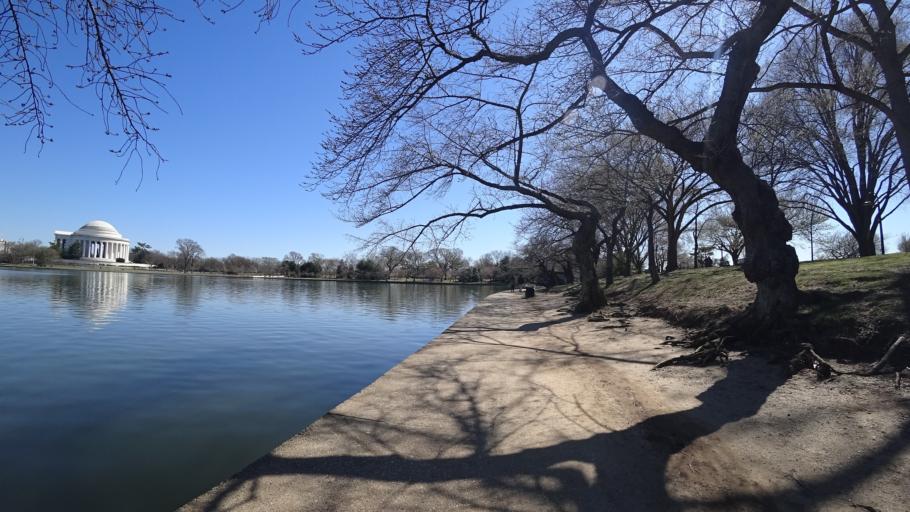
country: US
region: Washington, D.C.
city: Washington, D.C.
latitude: 38.8815
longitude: -77.0408
